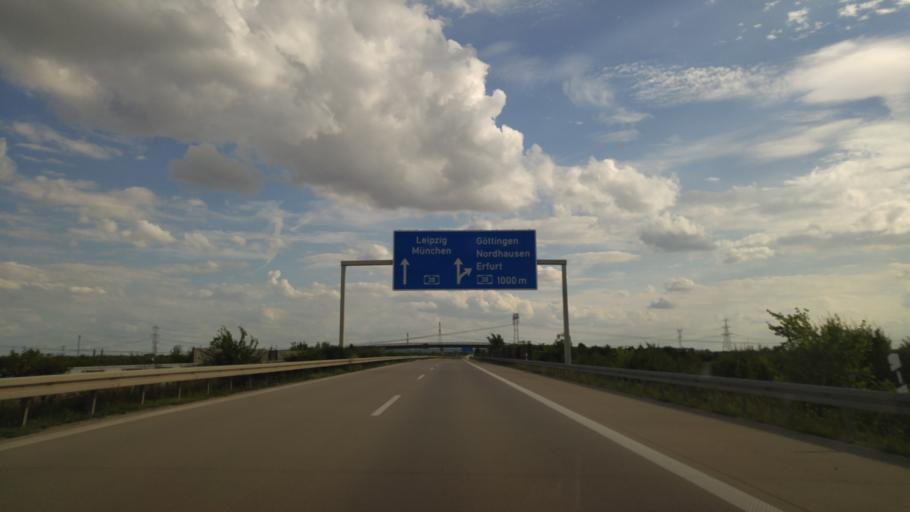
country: DE
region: Saxony-Anhalt
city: Bad Lauchstadt
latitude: 51.4171
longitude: 11.8621
